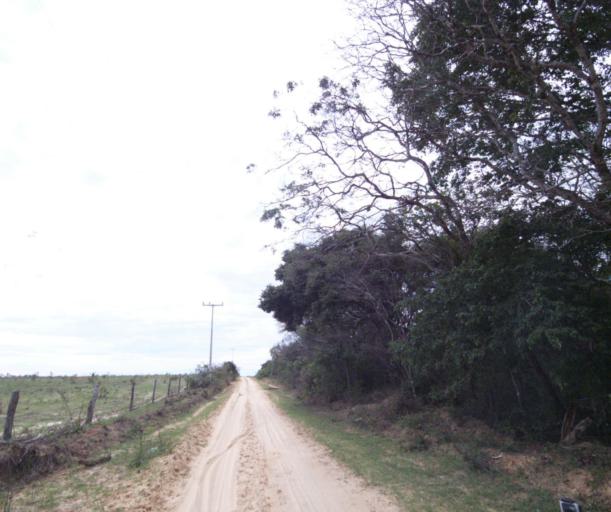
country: BR
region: Bahia
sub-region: Carinhanha
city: Carinhanha
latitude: -14.2527
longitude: -44.3656
